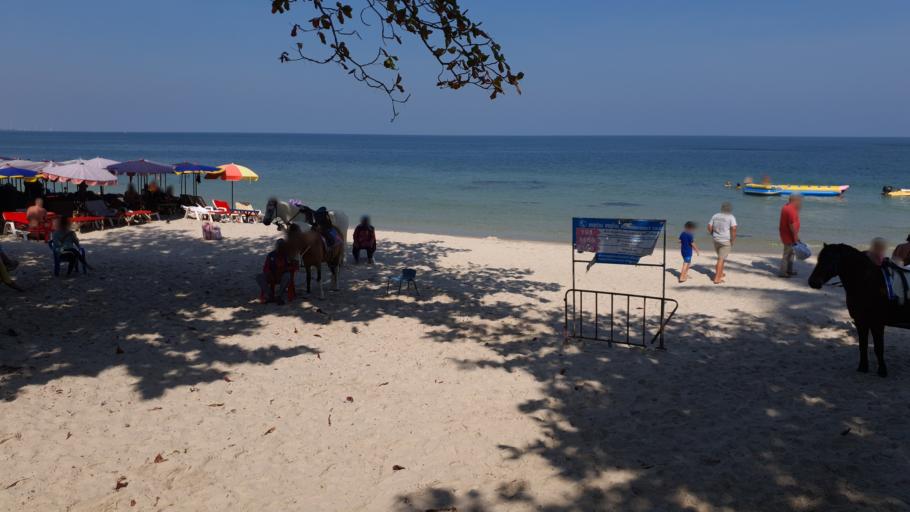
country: TH
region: Prachuap Khiri Khan
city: Hua Hin
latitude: 12.5695
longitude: 99.9627
